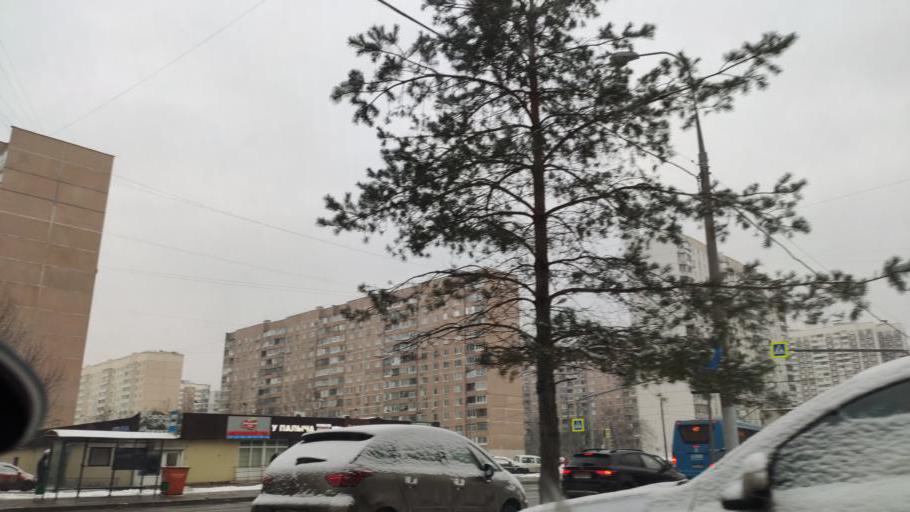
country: RU
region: Moscow
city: Novo-Peredelkino
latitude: 55.6413
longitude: 37.3458
